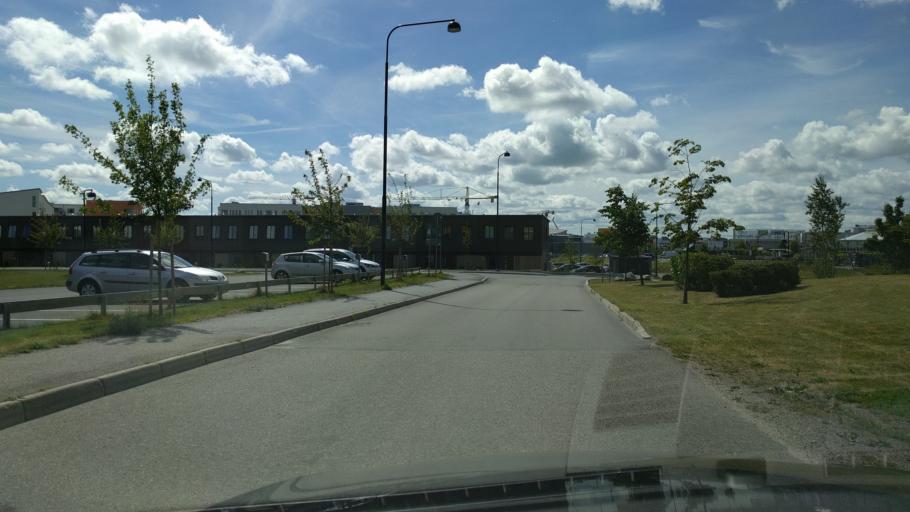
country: SE
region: Stockholm
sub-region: Jarfalla Kommun
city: Jakobsberg
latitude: 59.4176
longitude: 17.8644
